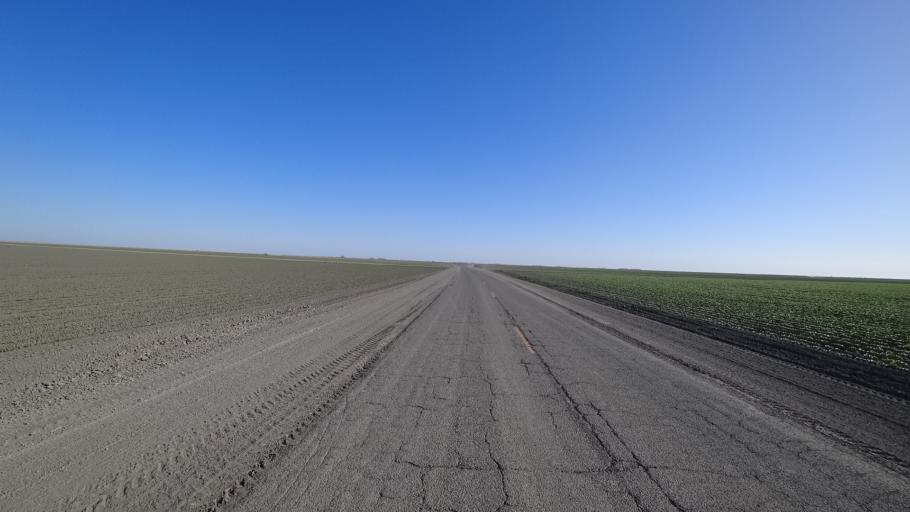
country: US
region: California
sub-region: Kings County
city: Stratford
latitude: 36.1072
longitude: -119.7979
